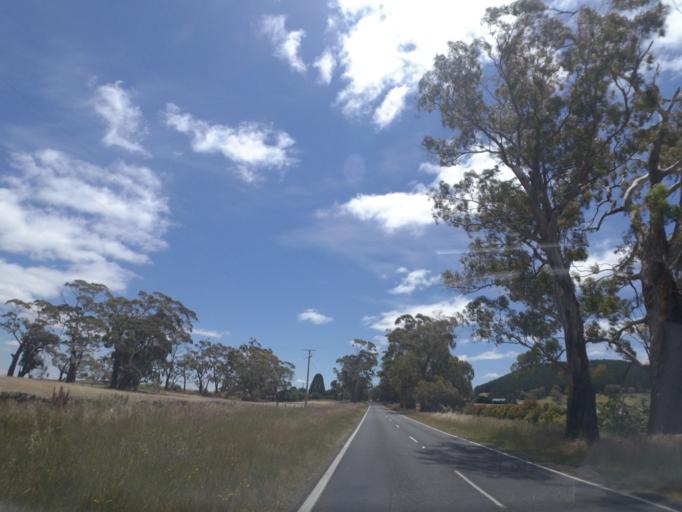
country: AU
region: Victoria
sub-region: Mount Alexander
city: Castlemaine
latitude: -37.2771
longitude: 144.1488
